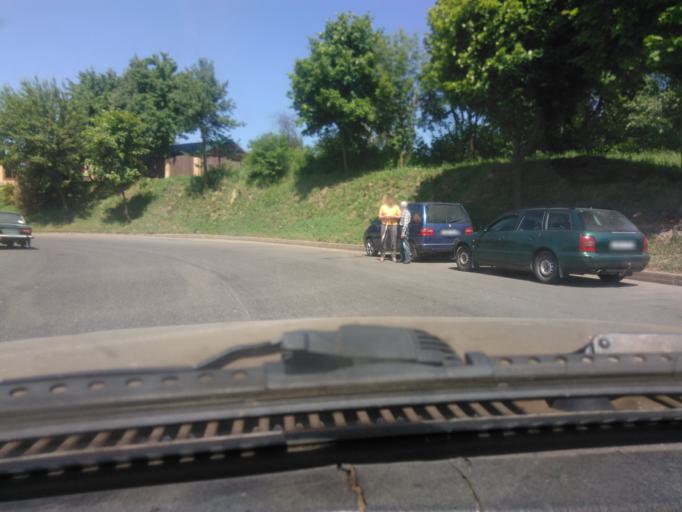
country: BY
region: Mogilev
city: Mahilyow
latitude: 53.9183
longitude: 30.3768
